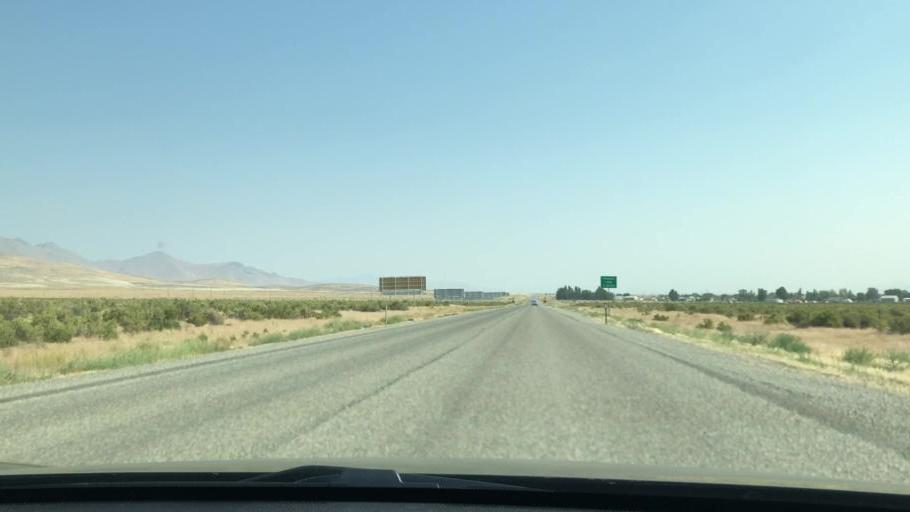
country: US
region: Nevada
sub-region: Humboldt County
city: Winnemucca
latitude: 41.0665
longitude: -117.7130
